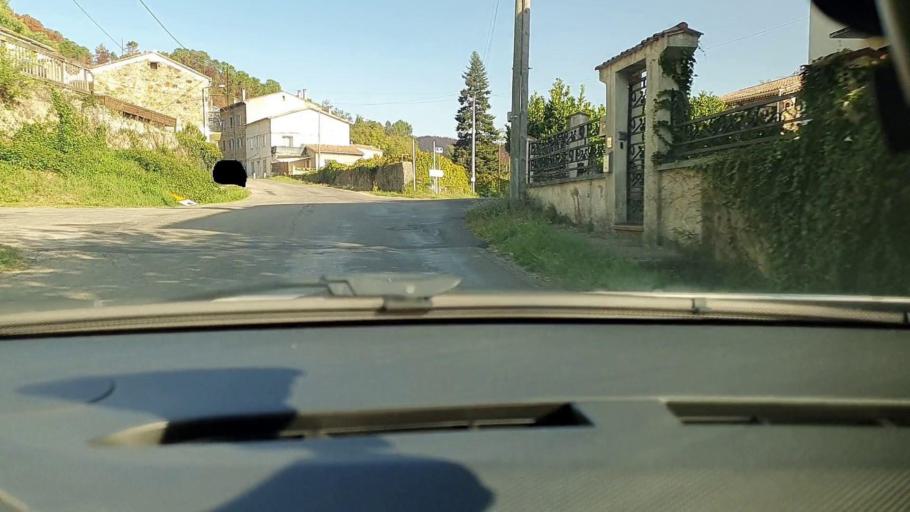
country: FR
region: Languedoc-Roussillon
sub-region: Departement du Gard
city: Besseges
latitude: 44.3008
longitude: 4.0932
